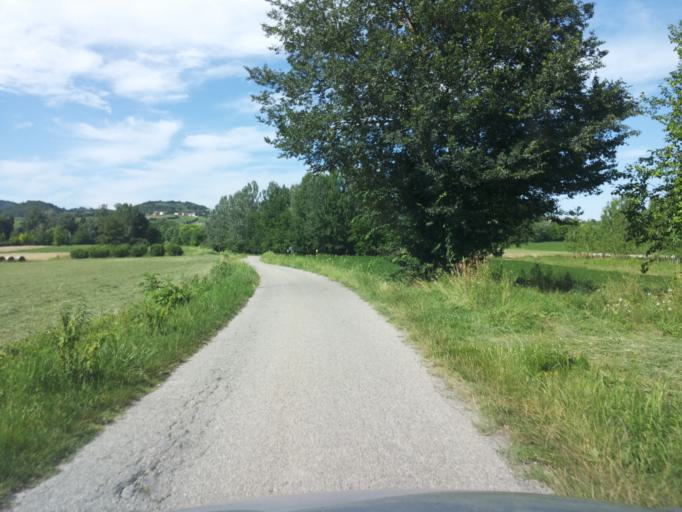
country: IT
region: Piedmont
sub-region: Provincia di Alessandria
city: Serralunga di Crea
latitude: 45.1069
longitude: 8.2730
